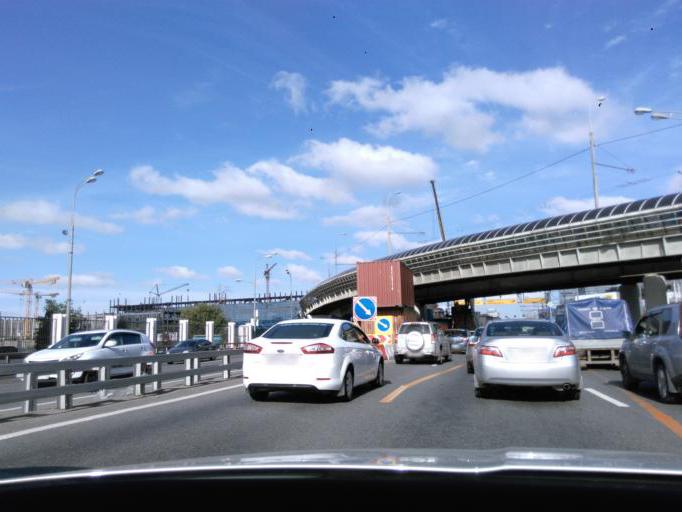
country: RU
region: Moskovskaya
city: Kozhukhovo
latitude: 55.7033
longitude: 37.6522
